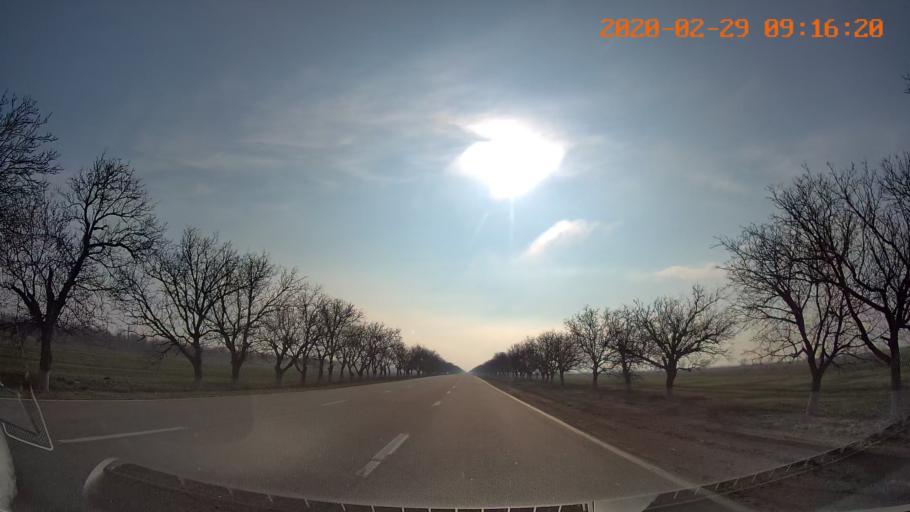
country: MD
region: Telenesti
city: Pervomaisc
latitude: 46.7928
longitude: 29.8845
